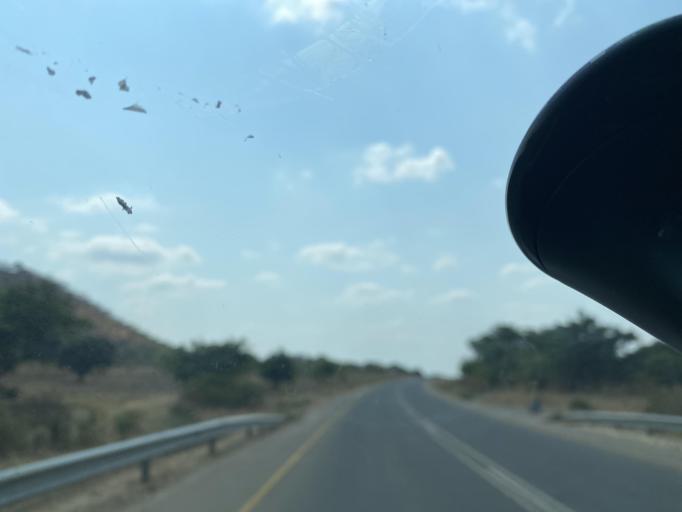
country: ZM
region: Lusaka
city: Chongwe
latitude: -15.5956
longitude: 28.7190
